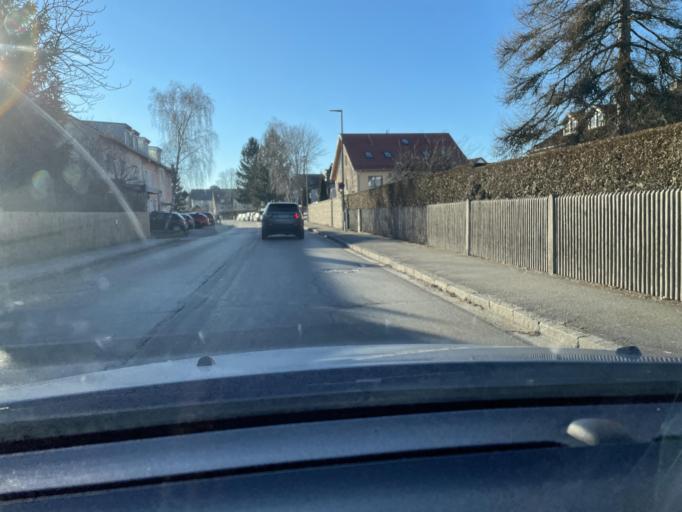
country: DE
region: Bavaria
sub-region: Upper Bavaria
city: Olching
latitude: 48.2164
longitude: 11.3246
